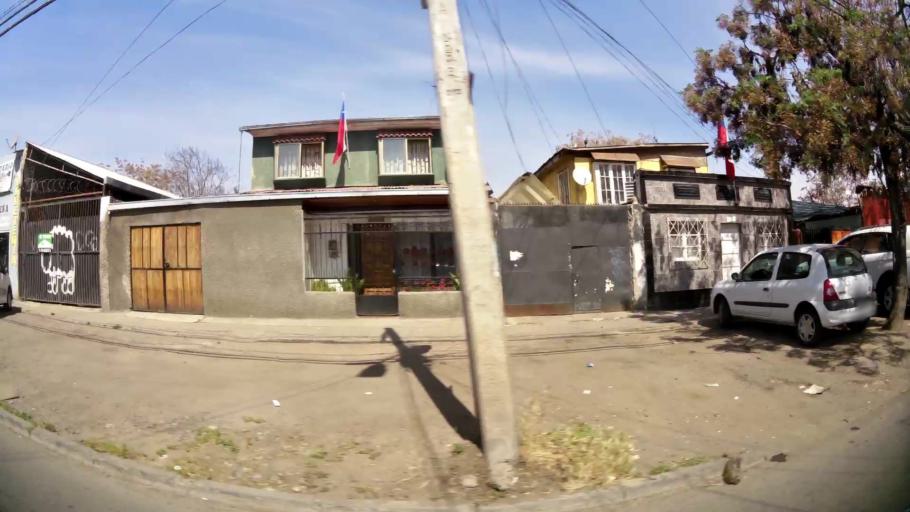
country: CL
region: Santiago Metropolitan
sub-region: Provincia de Santiago
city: Lo Prado
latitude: -33.4206
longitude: -70.7251
